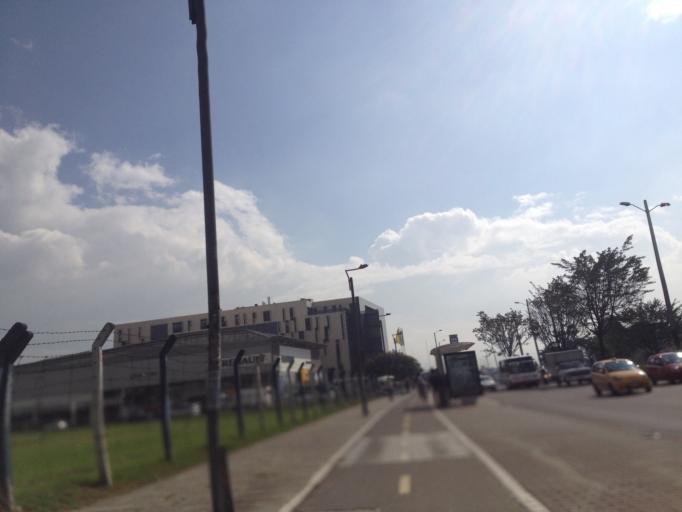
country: CO
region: Bogota D.C.
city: Bogota
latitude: 4.6831
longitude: -74.1152
